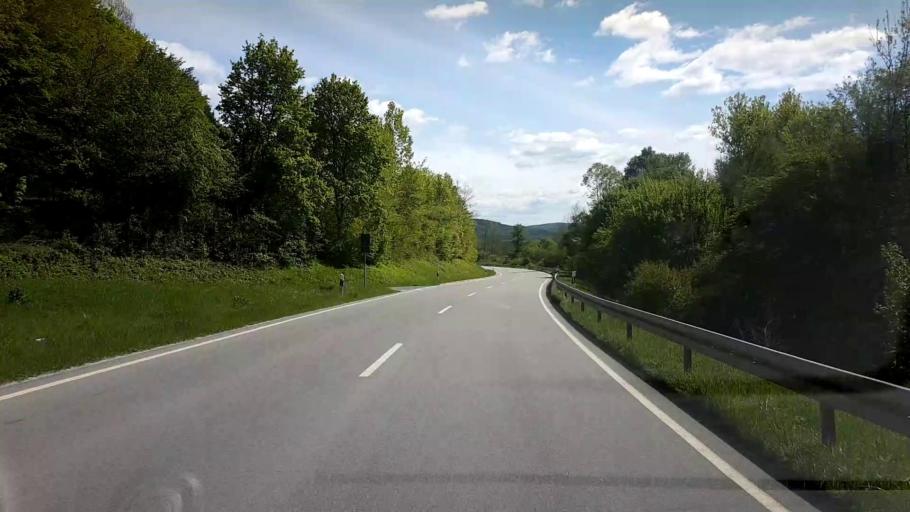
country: DE
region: Bavaria
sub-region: Upper Franconia
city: Ebermannstadt
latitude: 49.7947
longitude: 11.1770
